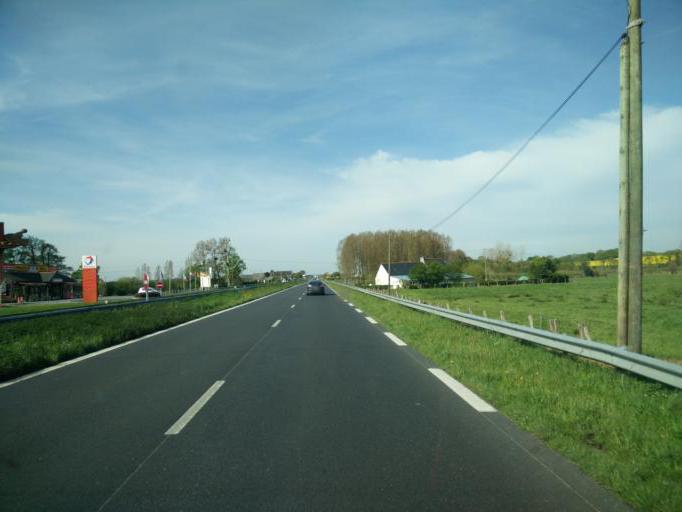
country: FR
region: Lower Normandy
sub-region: Departement de la Manche
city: Pontorson
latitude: 48.5738
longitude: -1.4570
